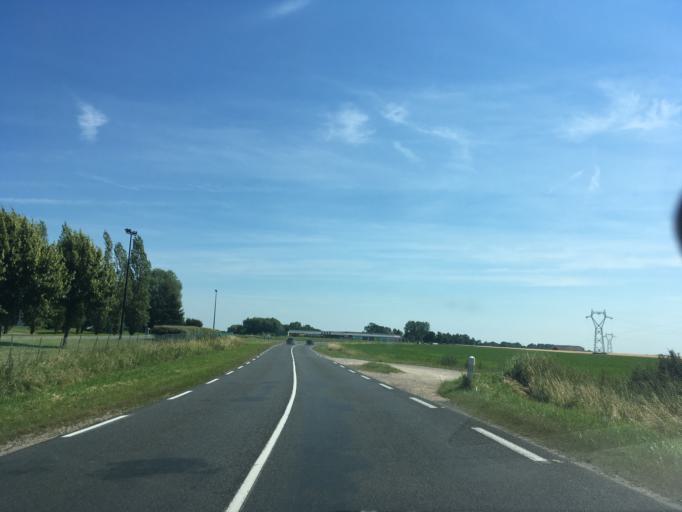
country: FR
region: Ile-de-France
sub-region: Departement de Seine-et-Marne
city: Bailly-Romainvilliers
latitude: 48.8498
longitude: 2.8375
